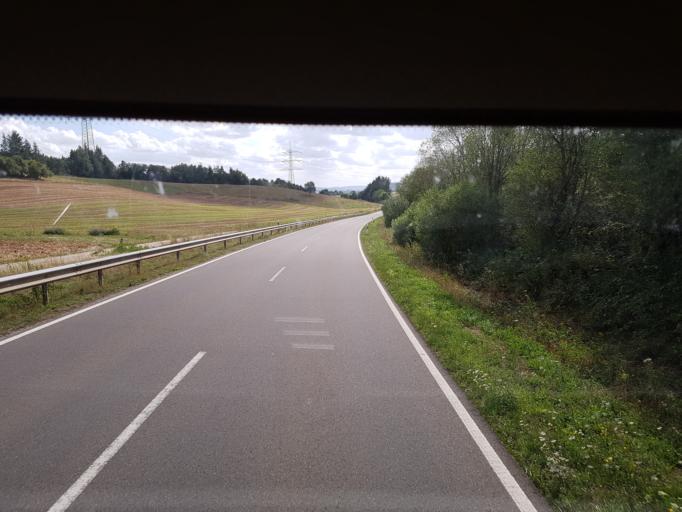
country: DE
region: Rheinland-Pfalz
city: Schweich
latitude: 49.8380
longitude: 6.7411
